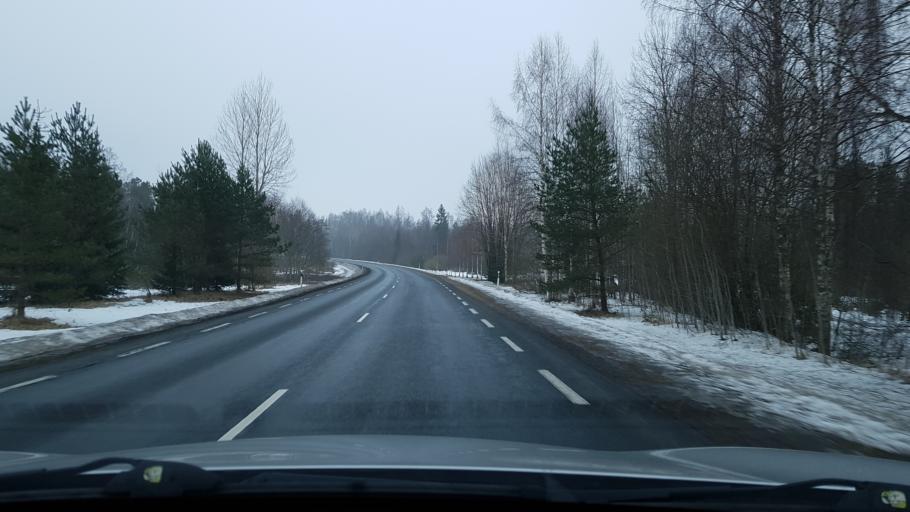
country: EE
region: Valgamaa
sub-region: Torva linn
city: Torva
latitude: 58.1214
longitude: 25.9928
